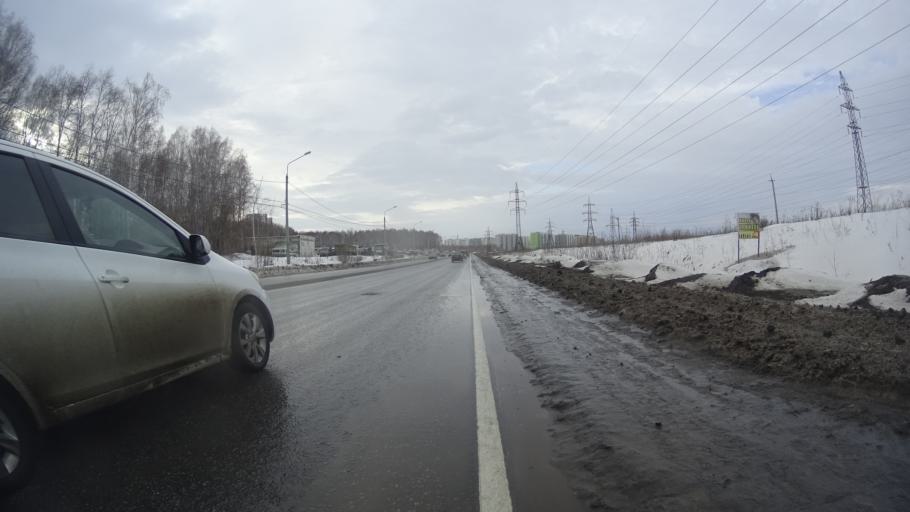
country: RU
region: Chelyabinsk
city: Roshchino
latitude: 55.2095
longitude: 61.3156
